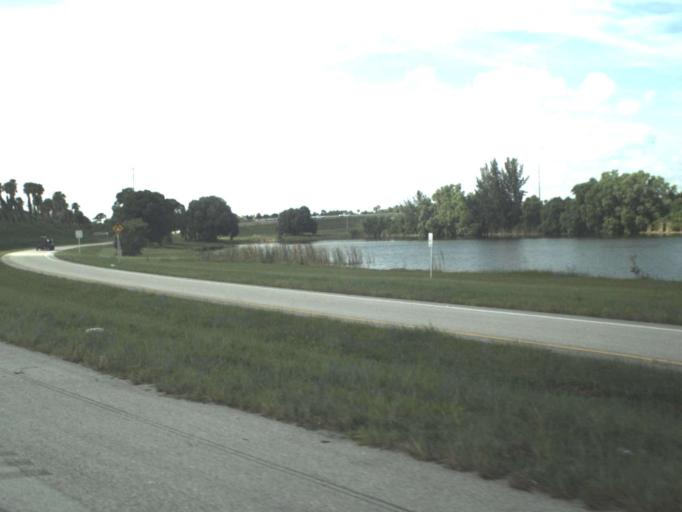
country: US
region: Florida
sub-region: Palm Beach County
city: Limestone Creek
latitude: 26.9388
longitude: -80.1515
